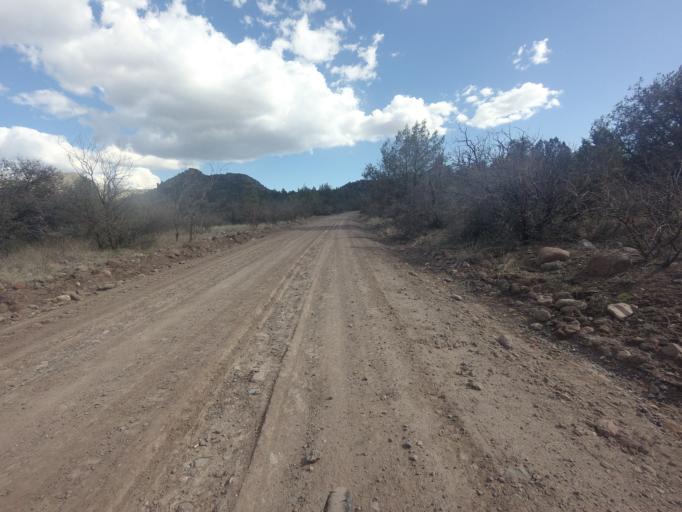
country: US
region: Arizona
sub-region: Yavapai County
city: Camp Verde
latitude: 34.4439
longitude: -111.6890
